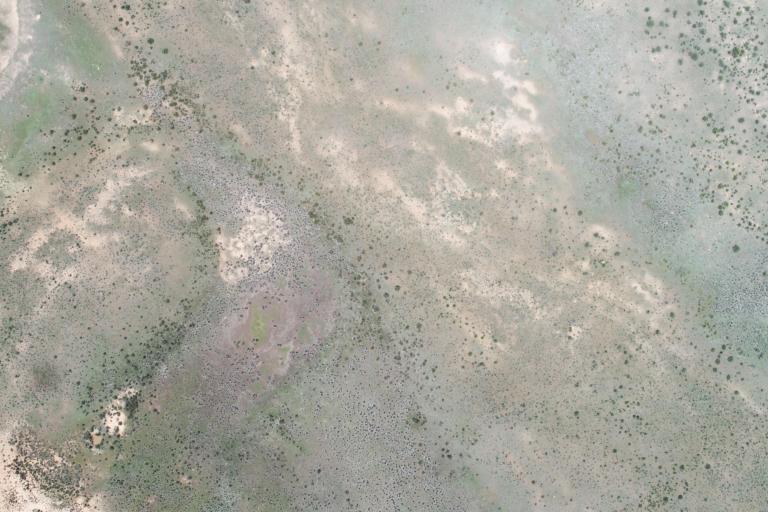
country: BO
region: La Paz
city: Curahuara de Carangas
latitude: -17.2826
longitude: -68.5158
